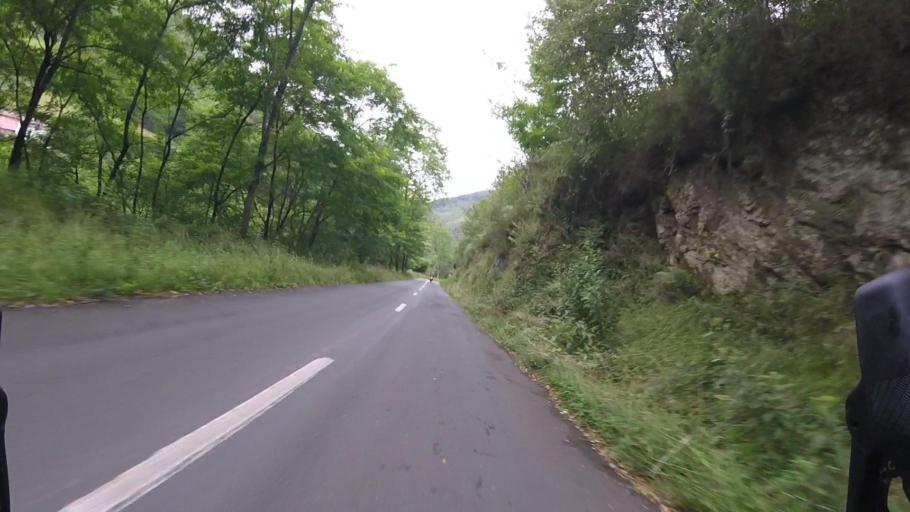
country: ES
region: Basque Country
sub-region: Provincia de Guipuzcoa
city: Irun
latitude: 43.2783
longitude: -1.8193
